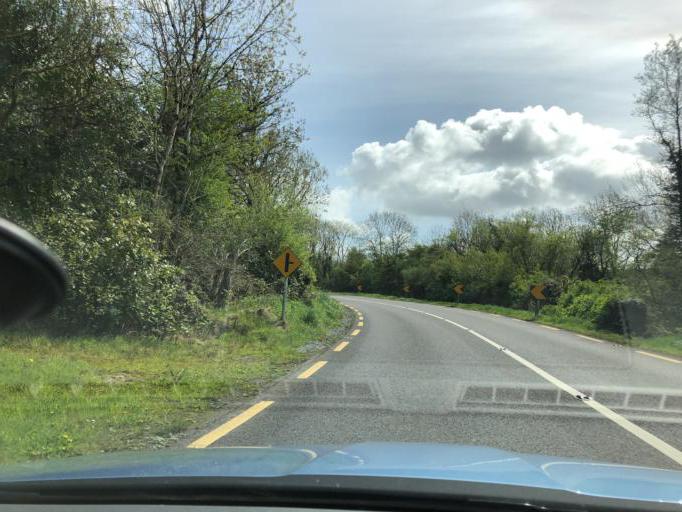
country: IE
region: Munster
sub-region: Ciarrai
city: Cill Airne
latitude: 52.0630
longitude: -9.3142
